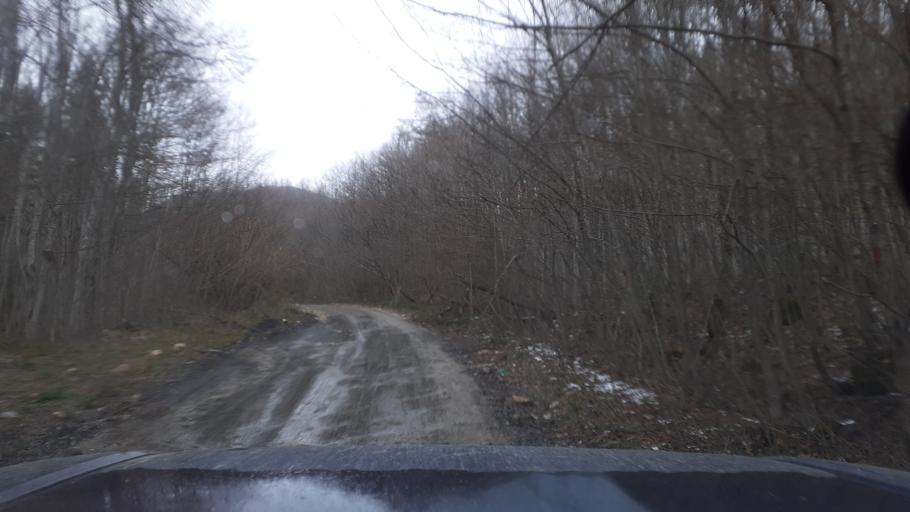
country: RU
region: Krasnodarskiy
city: Neftegorsk
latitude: 44.0805
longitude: 39.7295
